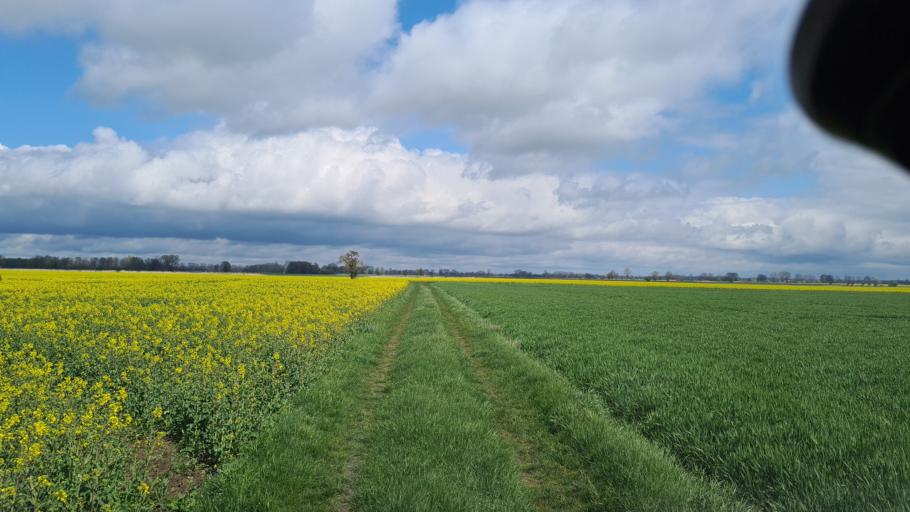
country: DE
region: Brandenburg
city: Doberlug-Kirchhain
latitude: 51.6607
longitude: 13.5297
